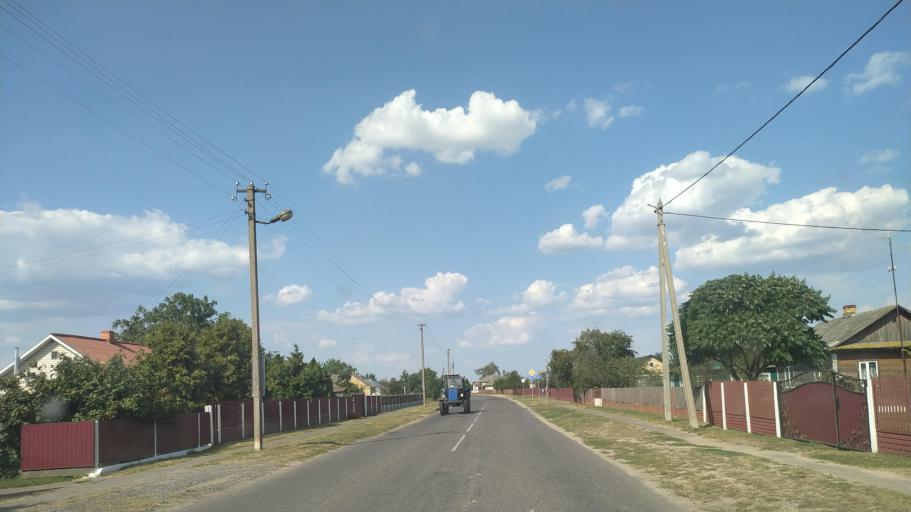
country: BY
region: Brest
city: Drahichyn
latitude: 52.1184
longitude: 25.1167
